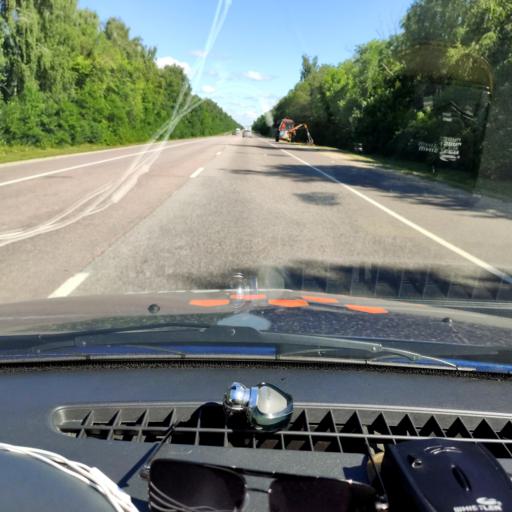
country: RU
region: Lipetsk
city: Khlevnoye
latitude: 52.2819
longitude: 39.1679
